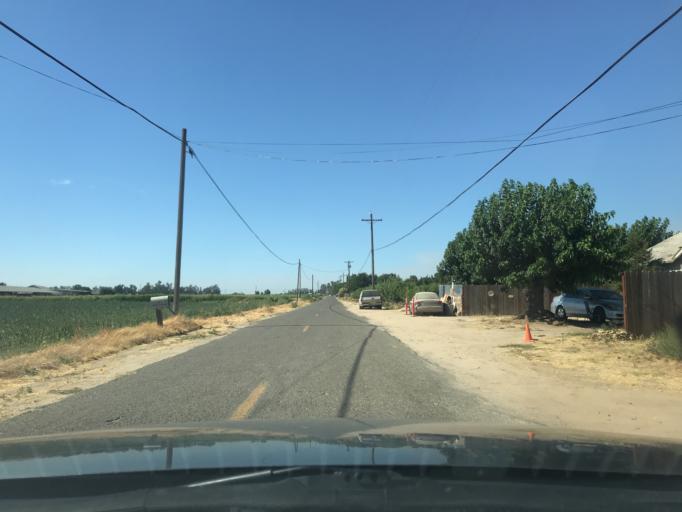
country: US
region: California
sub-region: Merced County
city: Atwater
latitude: 37.3284
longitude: -120.5500
